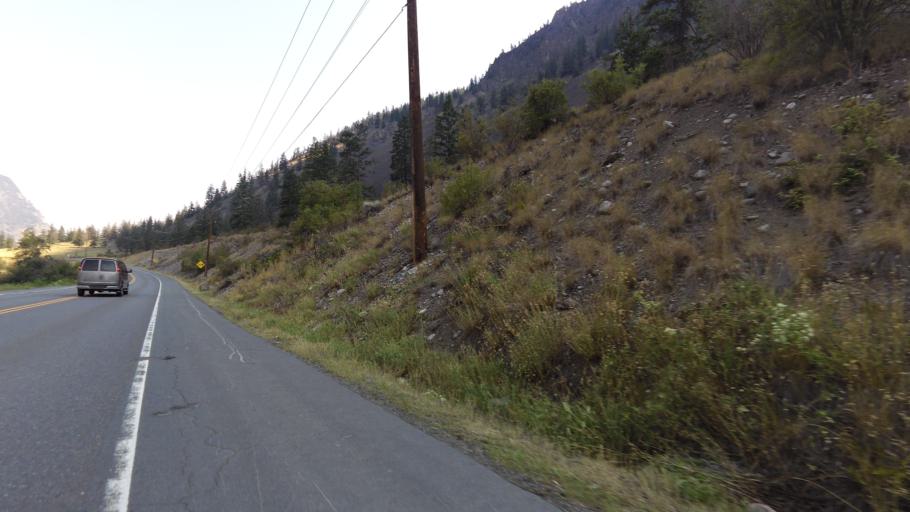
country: CA
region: British Columbia
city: Oliver
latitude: 49.2732
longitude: -120.0211
